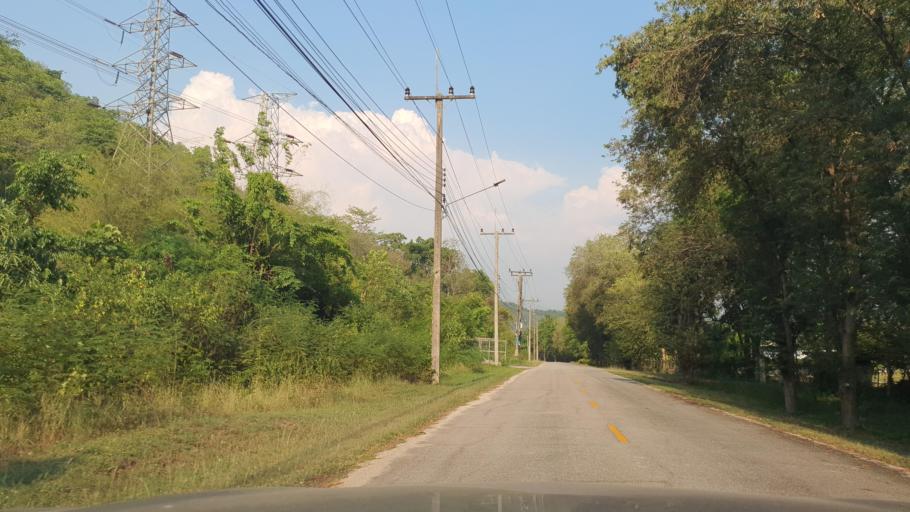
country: TH
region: Kanchanaburi
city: Sai Yok
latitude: 14.2255
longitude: 99.2272
